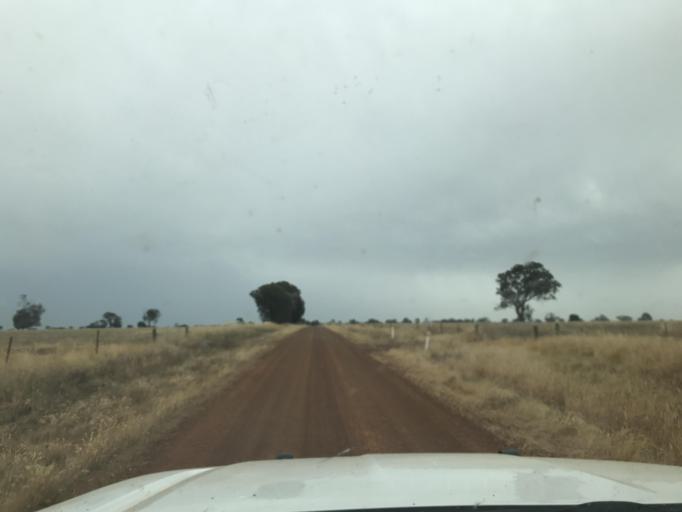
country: AU
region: Victoria
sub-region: Horsham
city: Horsham
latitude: -37.0640
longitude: 141.6461
